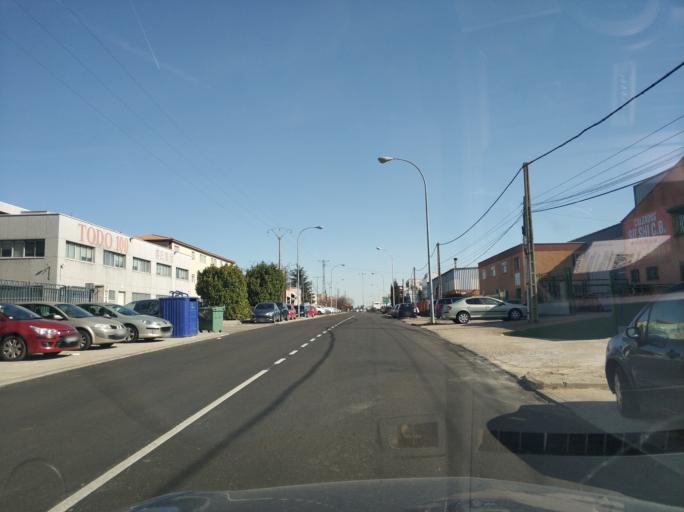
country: ES
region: Castille and Leon
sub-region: Provincia de Valladolid
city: Cisterniga
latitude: 41.6166
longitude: -4.7080
